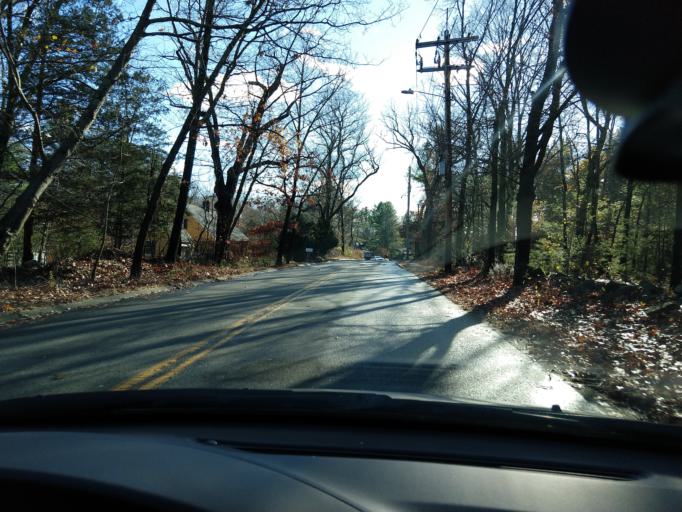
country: US
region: Massachusetts
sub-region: Middlesex County
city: Bedford
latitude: 42.4986
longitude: -71.2569
